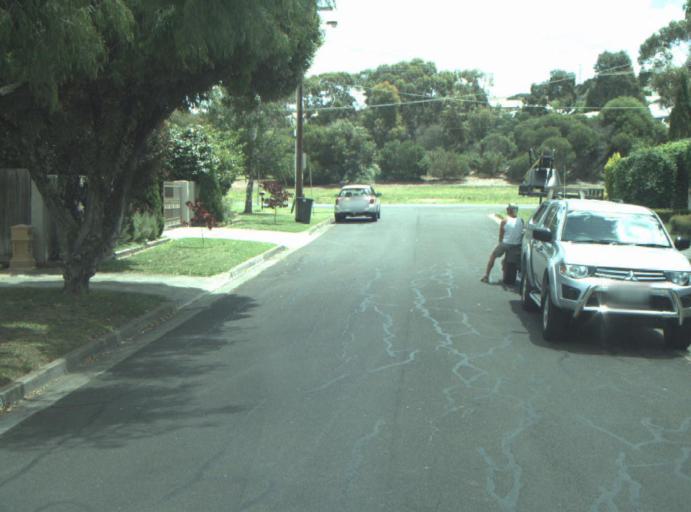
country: AU
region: Victoria
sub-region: Greater Geelong
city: Wandana Heights
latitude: -38.1778
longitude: 144.3126
